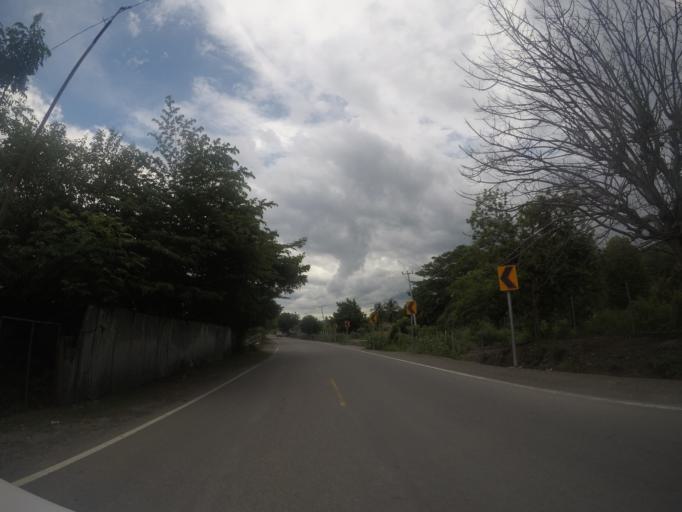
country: TL
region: Liquica
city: Liquica
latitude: -8.6051
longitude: 125.2934
